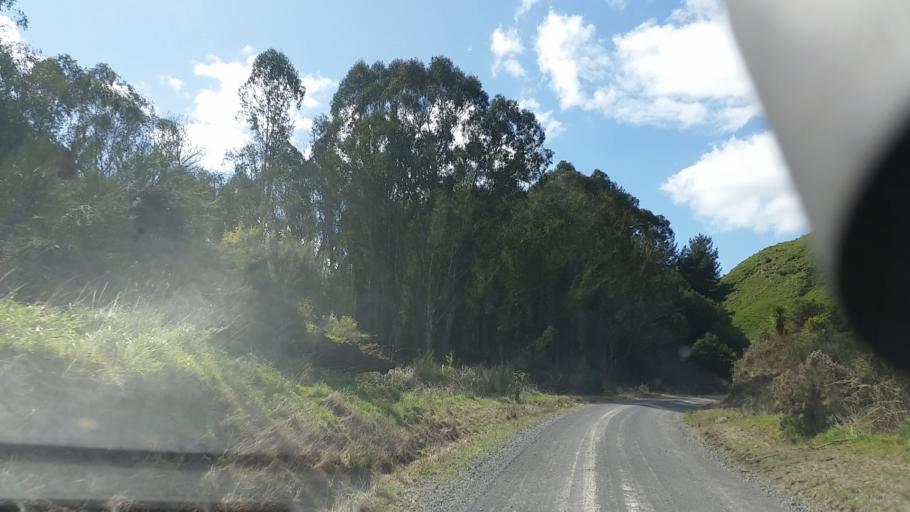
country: NZ
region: Waikato
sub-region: Taupo District
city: Taupo
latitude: -38.4911
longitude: 176.2074
